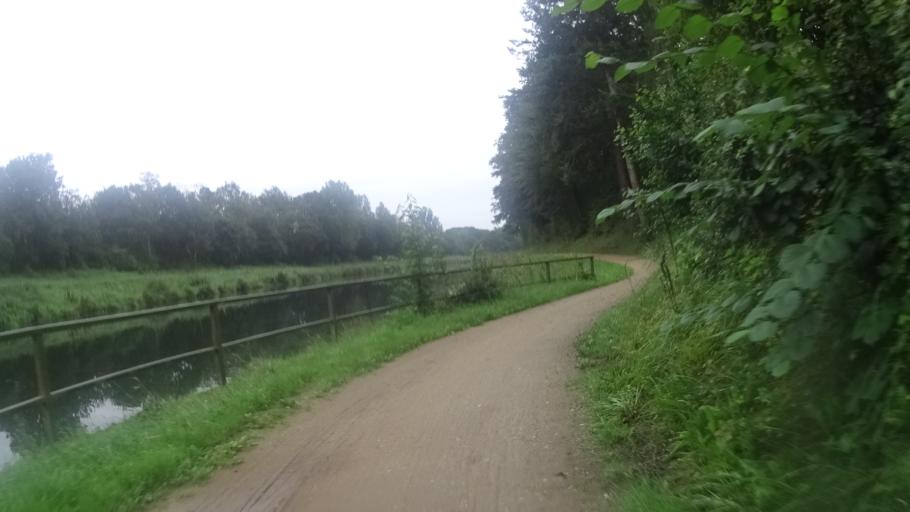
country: DE
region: Schleswig-Holstein
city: Grambek
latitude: 53.5820
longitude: 10.6708
